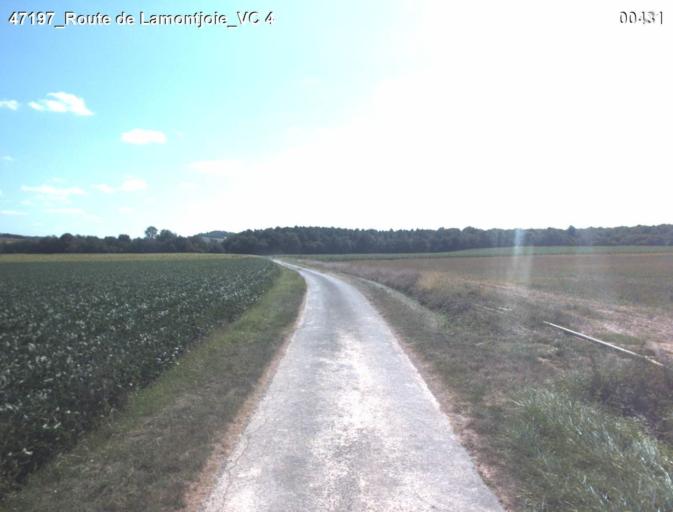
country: FR
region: Aquitaine
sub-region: Departement du Lot-et-Garonne
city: Laplume
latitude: 44.0704
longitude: 0.4905
